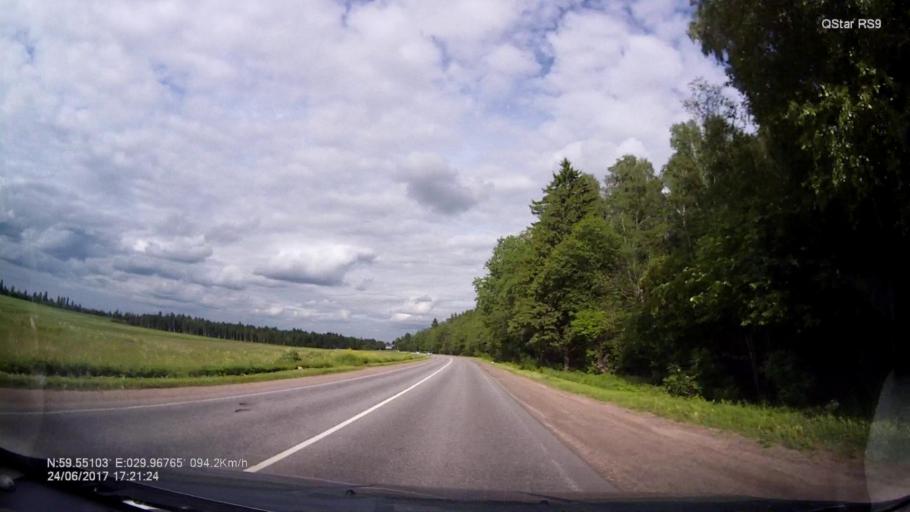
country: RU
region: Leningrad
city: Voyskovitsy
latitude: 59.5512
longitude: 29.9685
